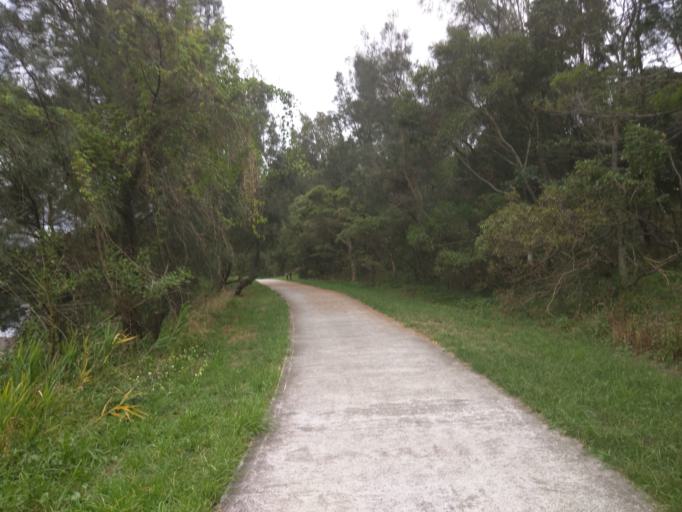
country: AU
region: New South Wales
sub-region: Wollongong
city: Berkeley
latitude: -34.4863
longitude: 150.8591
